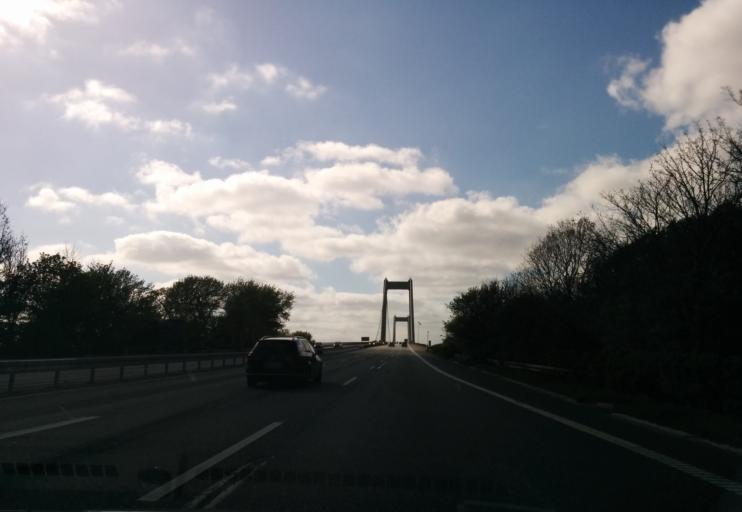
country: DK
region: South Denmark
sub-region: Middelfart Kommune
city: Strib
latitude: 55.5156
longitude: 9.7649
